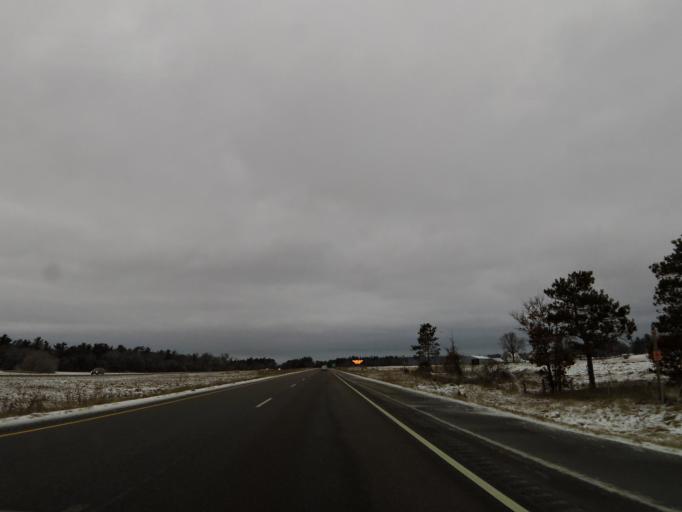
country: US
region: Wisconsin
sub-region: Eau Claire County
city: Altoona
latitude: 44.7412
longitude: -91.3758
